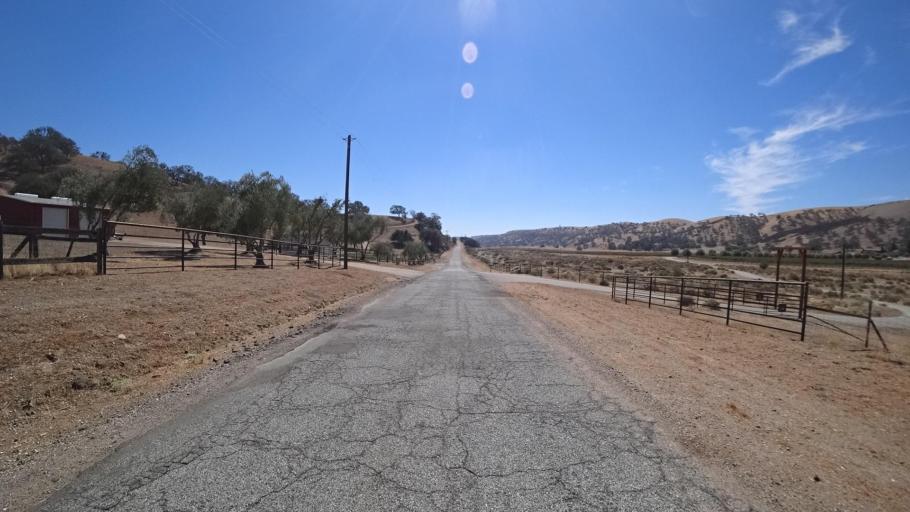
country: US
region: California
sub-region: San Luis Obispo County
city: San Miguel
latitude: 35.8956
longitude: -120.6997
